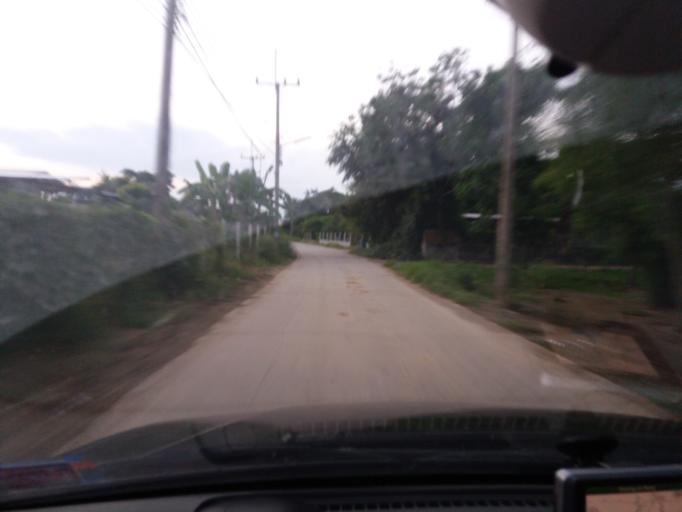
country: TH
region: Suphan Buri
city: Doembang Nangbuat
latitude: 14.8314
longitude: 100.1342
